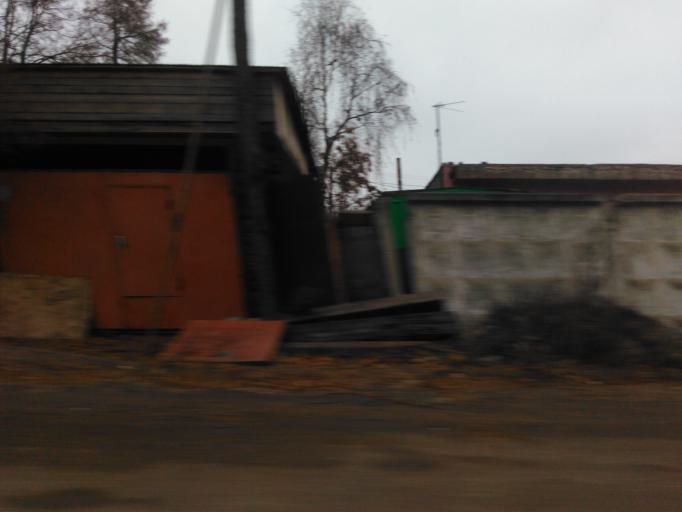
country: RU
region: Moskovskaya
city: Ashukino
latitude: 56.1296
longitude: 37.9762
